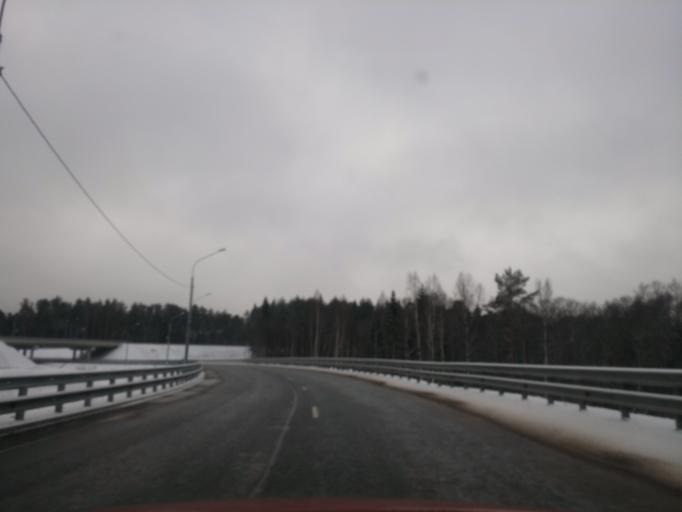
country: RU
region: Tverskaya
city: Likhoslavl'
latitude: 56.9464
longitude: 35.4946
